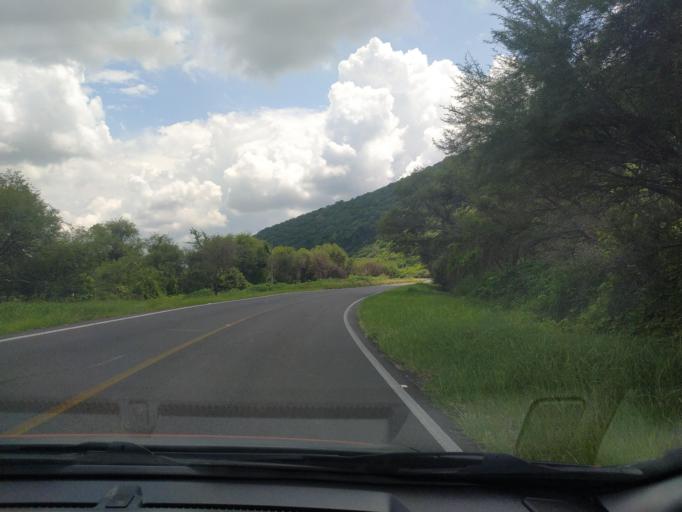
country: MX
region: Jalisco
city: Villa Corona
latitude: 20.3712
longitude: -103.6691
